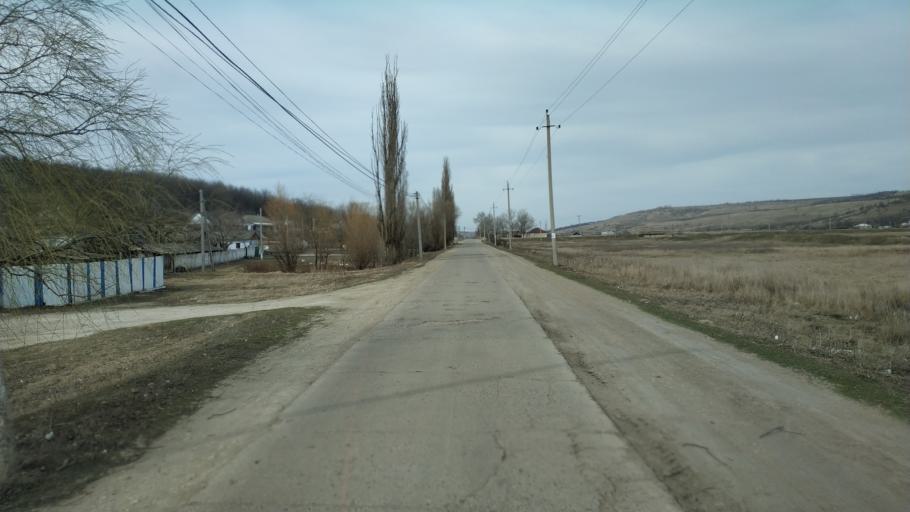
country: RO
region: Vaslui
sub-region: Comuna Dranceni
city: Dranceni
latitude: 46.8692
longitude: 28.1992
